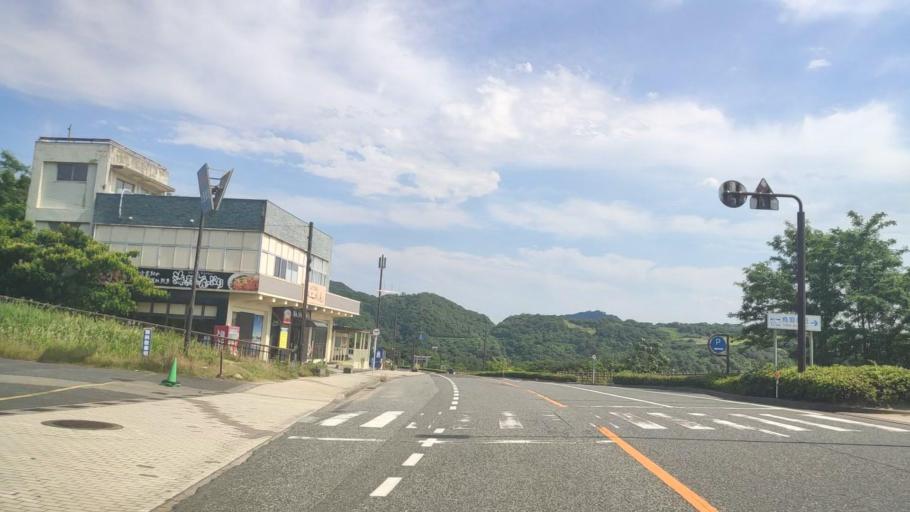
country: JP
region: Tottori
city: Tottori
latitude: 35.5411
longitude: 134.2365
